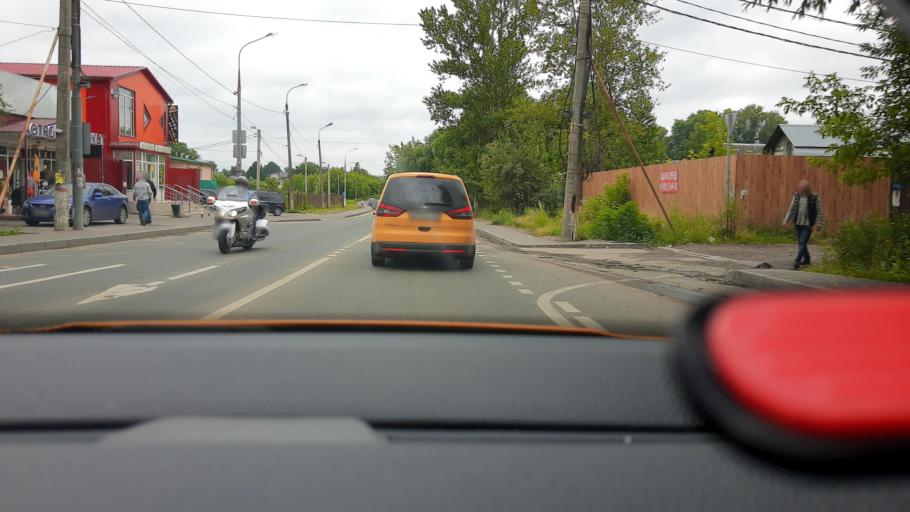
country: RU
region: Moskovskaya
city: Pirogovskiy
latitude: 55.9800
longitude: 37.7261
